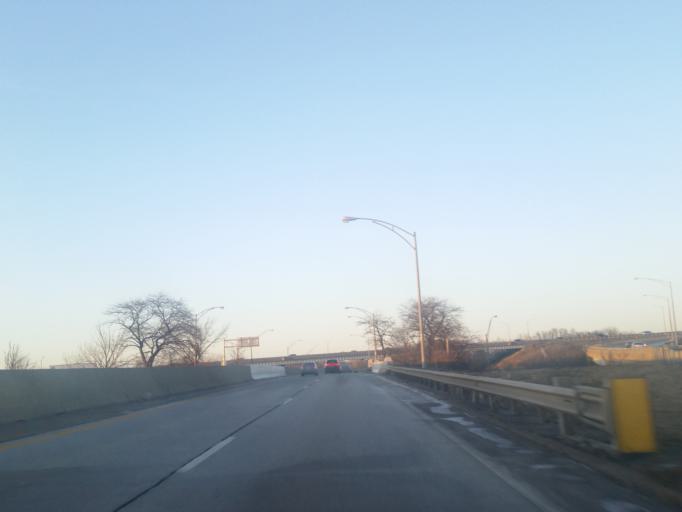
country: US
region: Ohio
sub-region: Cuyahoga County
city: Brook Park
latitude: 41.4179
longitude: -81.8291
